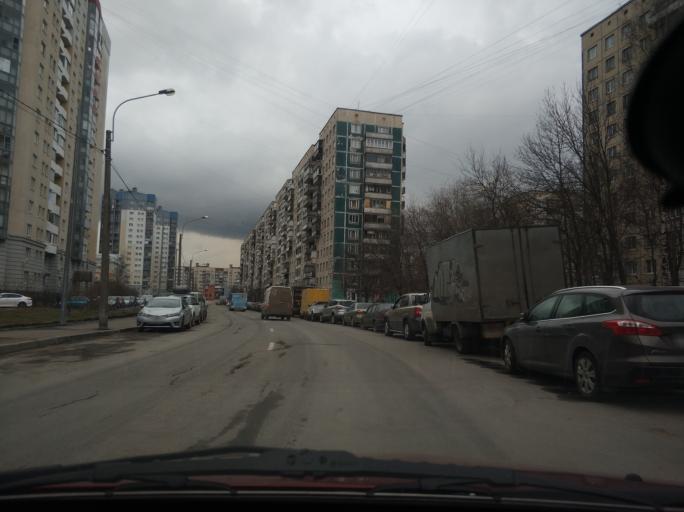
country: RU
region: St.-Petersburg
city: Krasnogvargeisky
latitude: 59.9461
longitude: 30.4844
